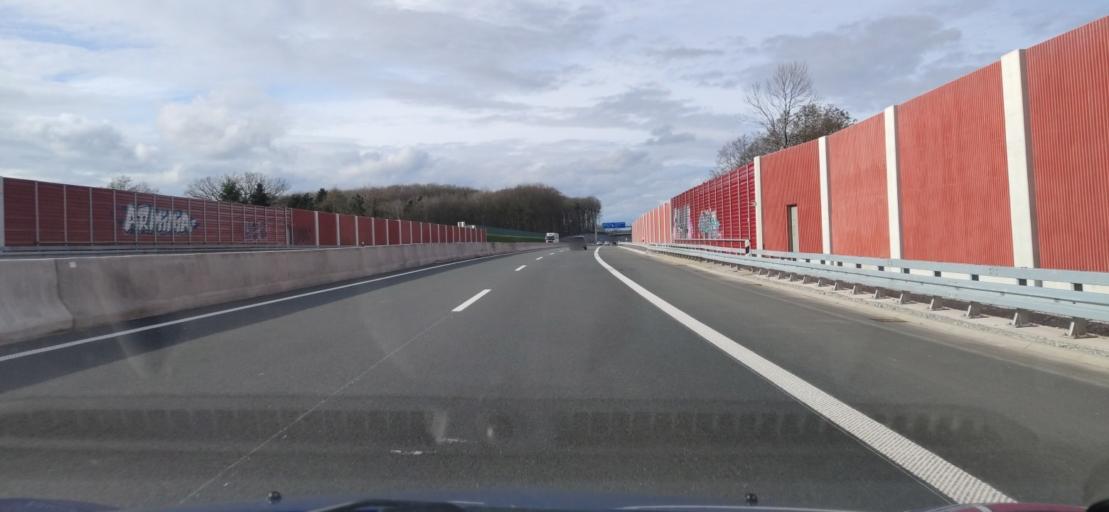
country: DE
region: North Rhine-Westphalia
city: Borgholzhausen
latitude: 52.0695
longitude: 8.2603
